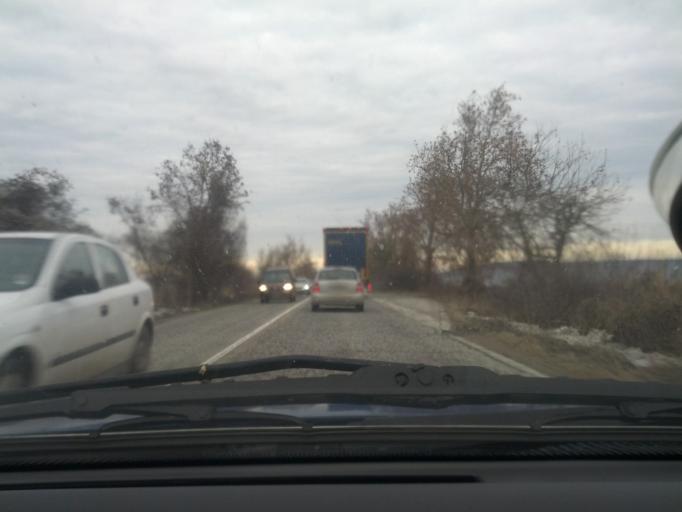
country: BG
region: Vratsa
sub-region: Obshtina Borovan
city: Borovan
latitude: 43.3234
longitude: 23.6851
